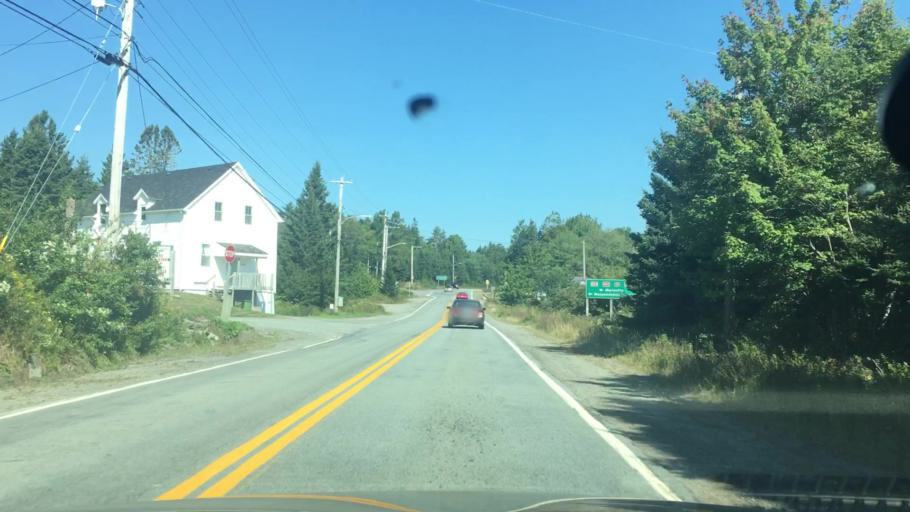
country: CA
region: Nova Scotia
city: New Glasgow
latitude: 44.9245
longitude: -62.5457
